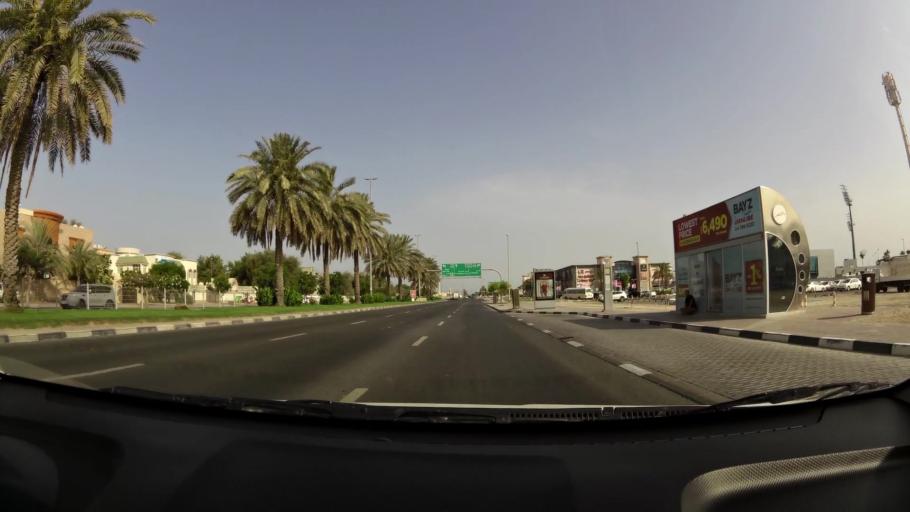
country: AE
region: Ash Shariqah
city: Sharjah
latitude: 25.2877
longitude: 55.3486
